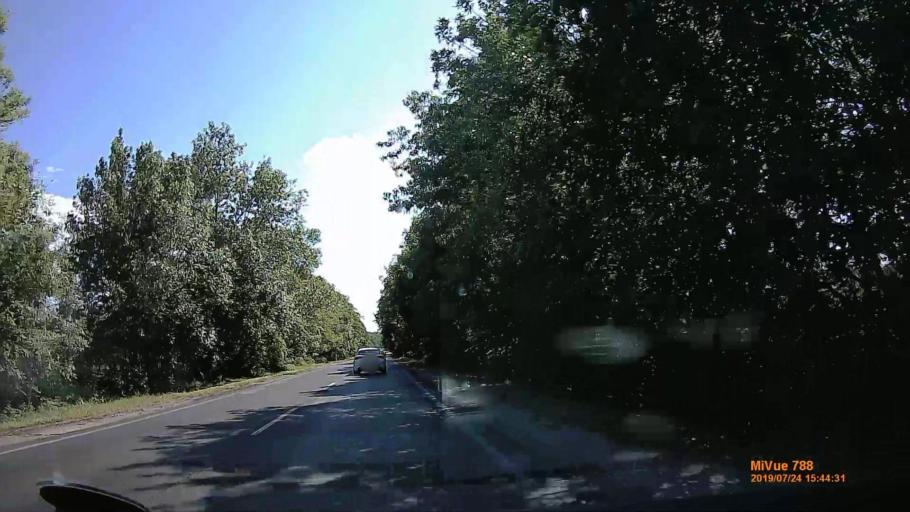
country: HU
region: Szabolcs-Szatmar-Bereg
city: Vasarosnameny
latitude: 48.0988
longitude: 22.2931
